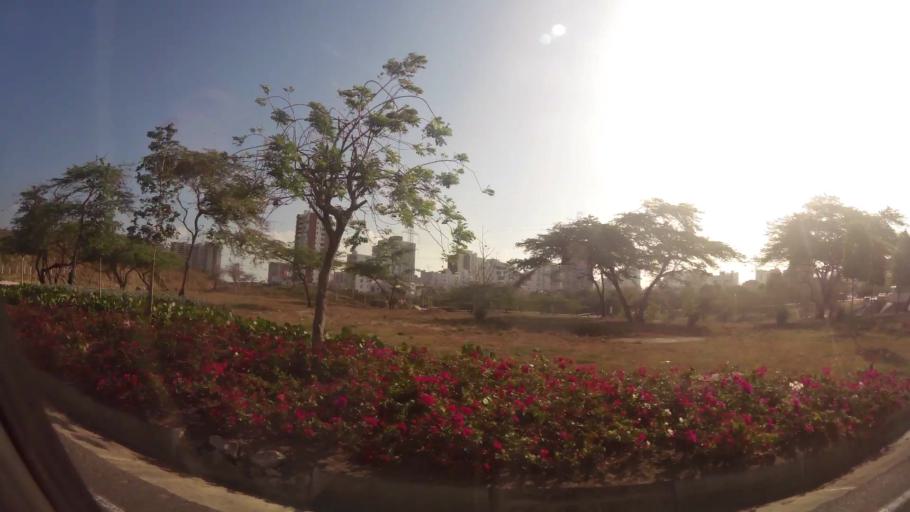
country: CO
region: Atlantico
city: Barranquilla
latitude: 11.0123
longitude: -74.8411
